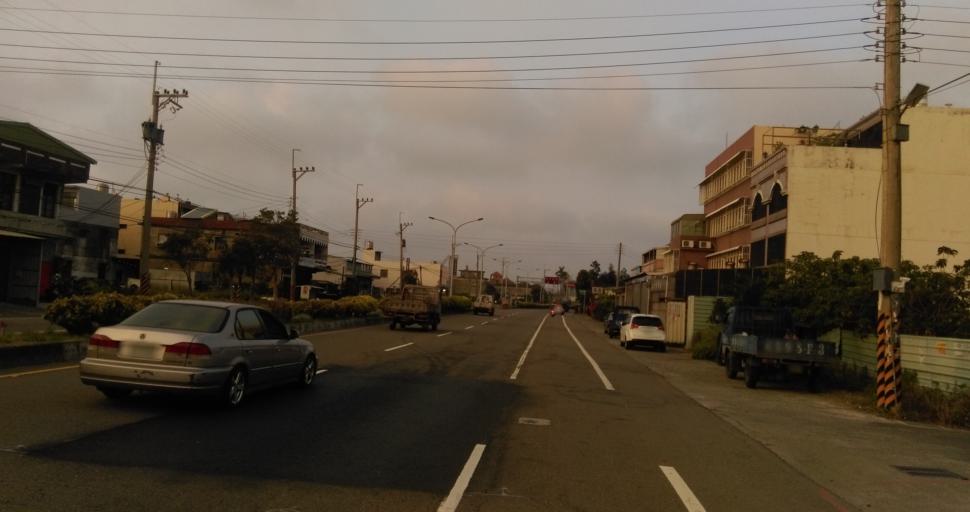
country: TW
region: Taiwan
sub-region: Hsinchu
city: Hsinchu
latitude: 24.8162
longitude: 120.9233
